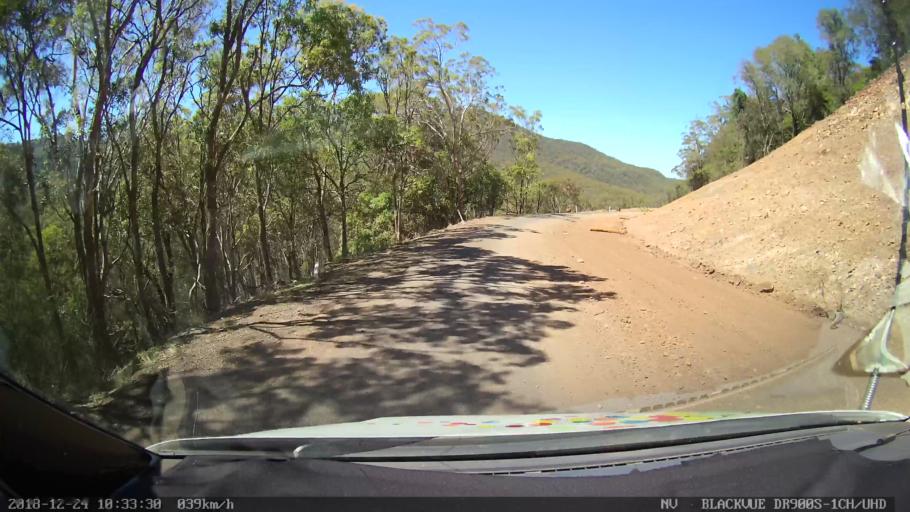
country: AU
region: New South Wales
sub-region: Upper Hunter Shire
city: Merriwa
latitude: -31.8419
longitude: 150.5103
